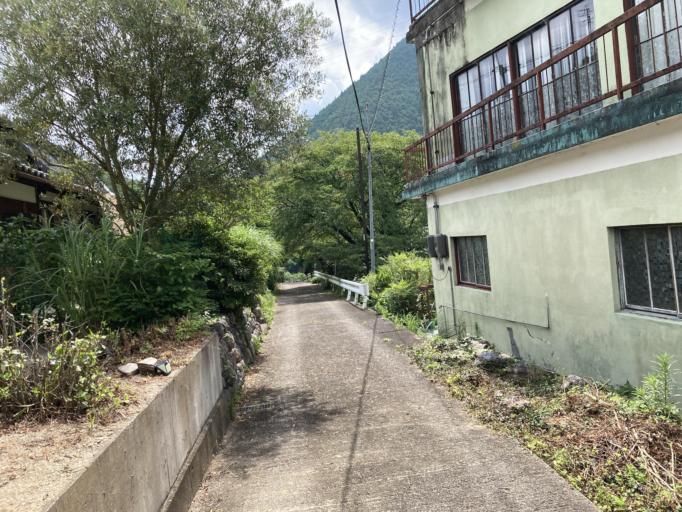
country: JP
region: Nara
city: Yoshino-cho
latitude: 34.3769
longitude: 135.8958
